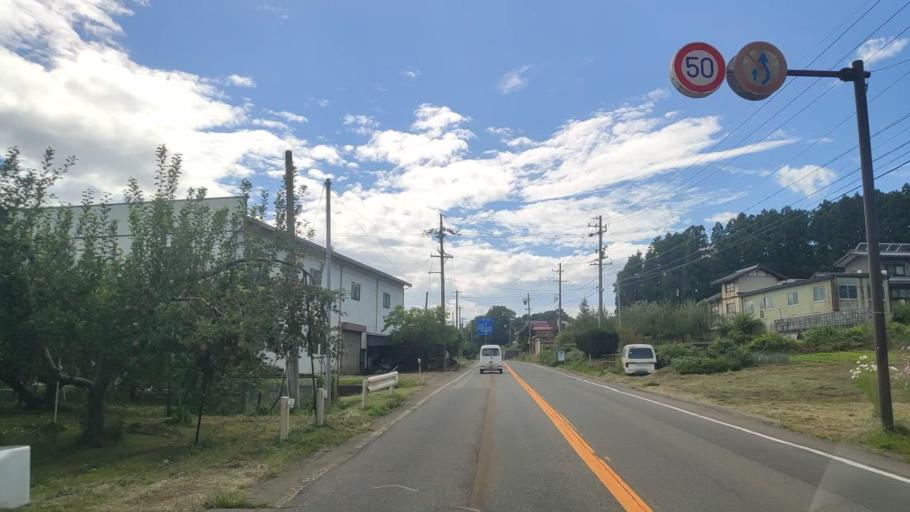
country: JP
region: Nagano
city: Nakano
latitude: 36.7615
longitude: 138.3180
